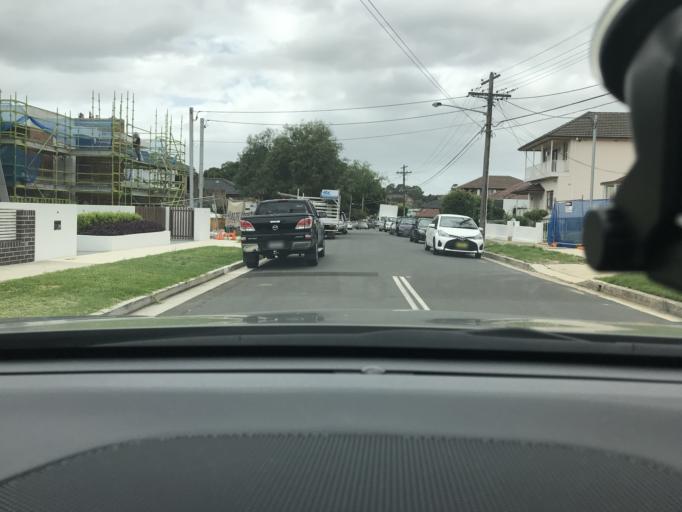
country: AU
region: New South Wales
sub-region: Canada Bay
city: Wareemba
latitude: -33.8633
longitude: 151.1251
